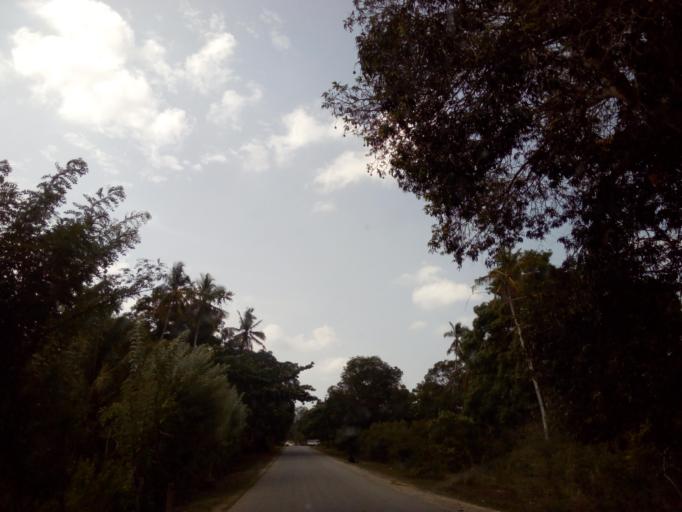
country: TZ
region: Zanzibar Central/South
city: Mahonda
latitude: -6.2988
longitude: 39.3731
